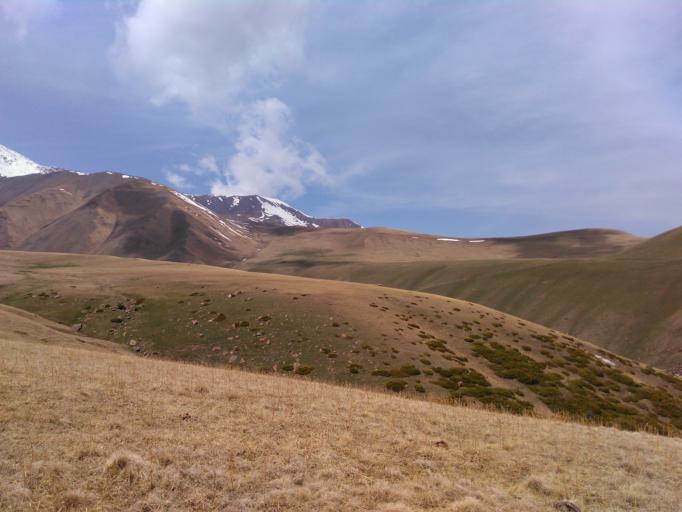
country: KG
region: Chuy
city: Bystrovka
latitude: 42.5120
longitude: 75.6320
